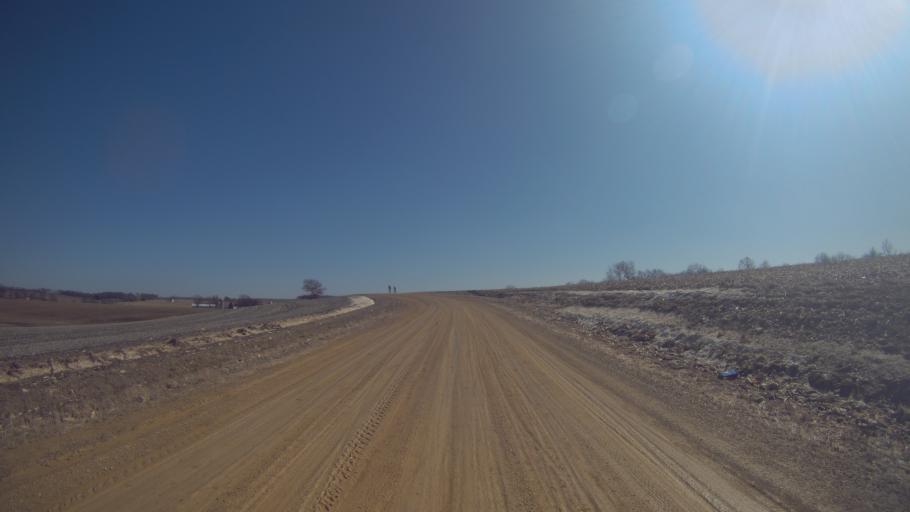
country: US
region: Illinois
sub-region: Winnebago County
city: Lake Summerset
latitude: 42.3876
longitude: -89.4396
